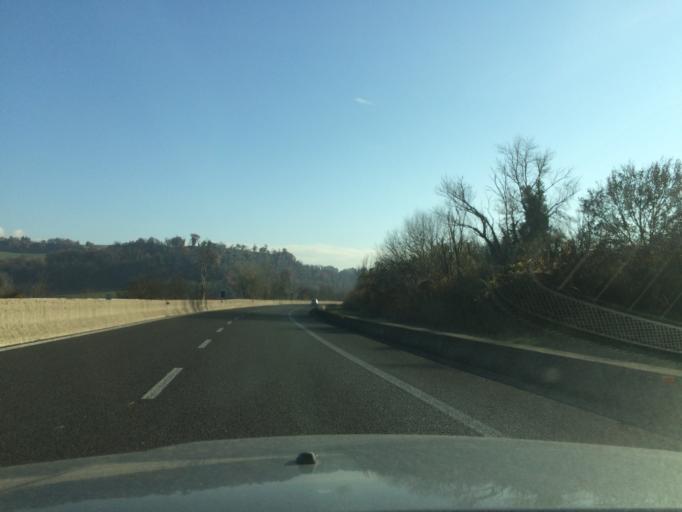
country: IT
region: Umbria
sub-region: Provincia di Perugia
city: Todi
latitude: 42.7787
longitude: 12.4432
